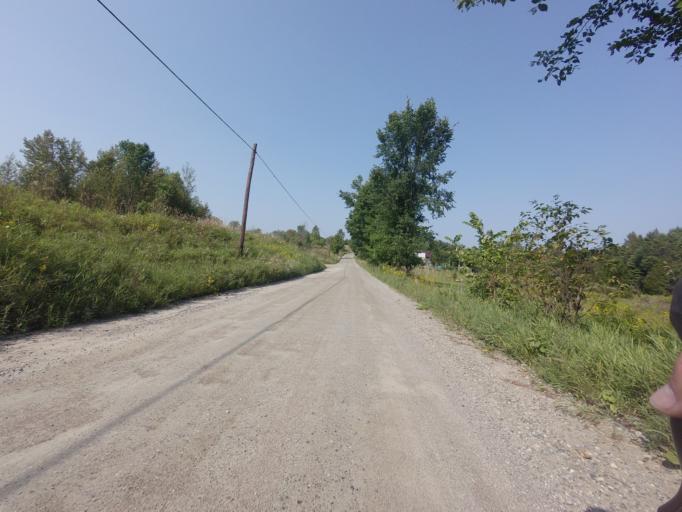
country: CA
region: Ontario
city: Skatepark
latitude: 44.7666
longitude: -76.8142
